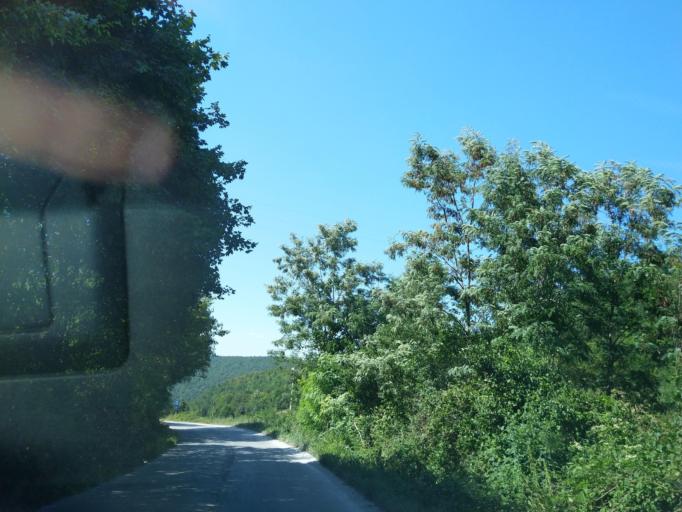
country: RS
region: Central Serbia
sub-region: Zlatiborski Okrug
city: Uzice
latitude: 43.8227
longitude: 19.8582
